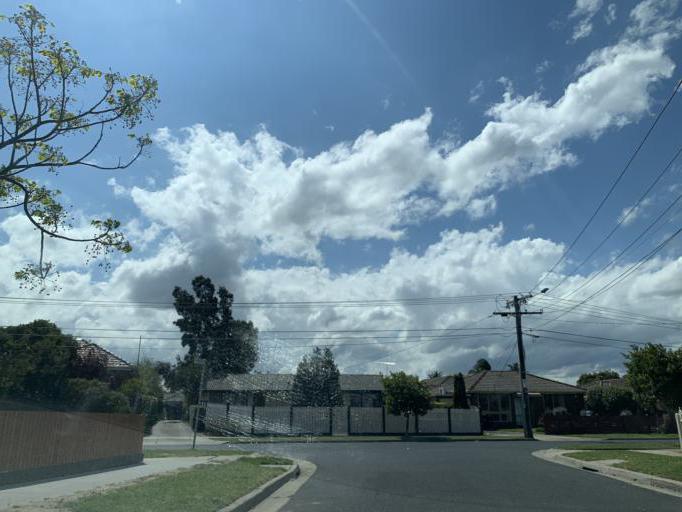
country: AU
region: Victoria
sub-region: Kingston
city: Mordialloc
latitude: -38.0046
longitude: 145.0942
